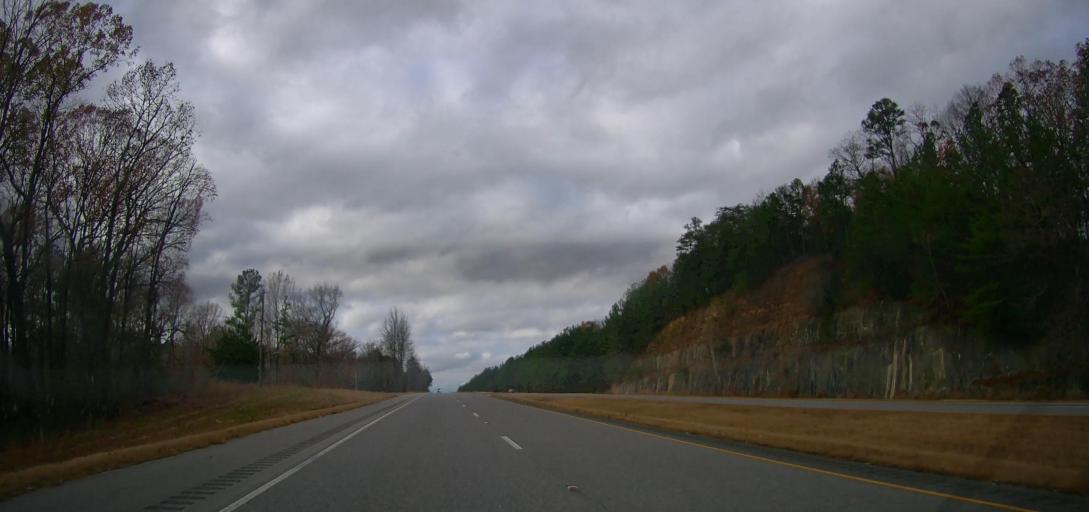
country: US
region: Alabama
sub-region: Lawrence County
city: Town Creek
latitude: 34.6161
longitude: -87.4632
